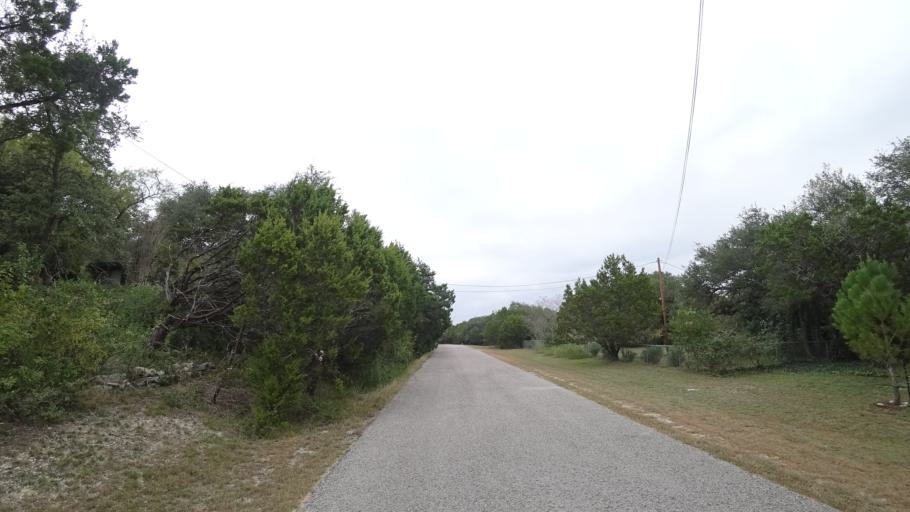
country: US
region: Texas
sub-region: Travis County
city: Barton Creek
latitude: 30.2621
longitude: -97.9157
